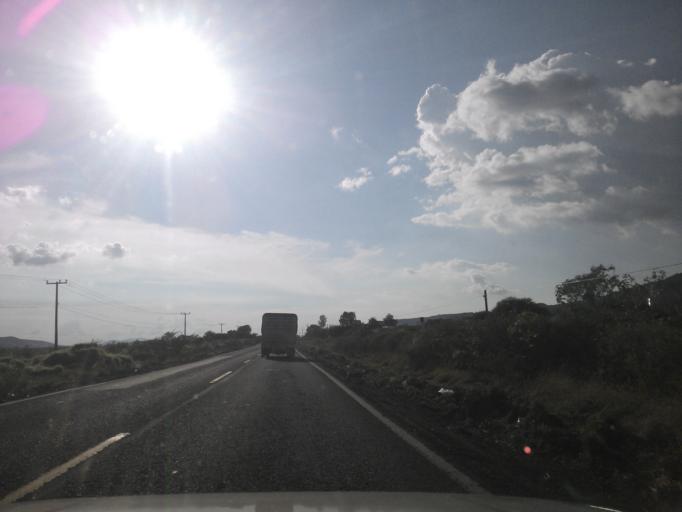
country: MX
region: Jalisco
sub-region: Atotonilco el Alto
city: Vistas del Maguey [Fraccionamiento]
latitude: 20.5414
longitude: -102.5746
